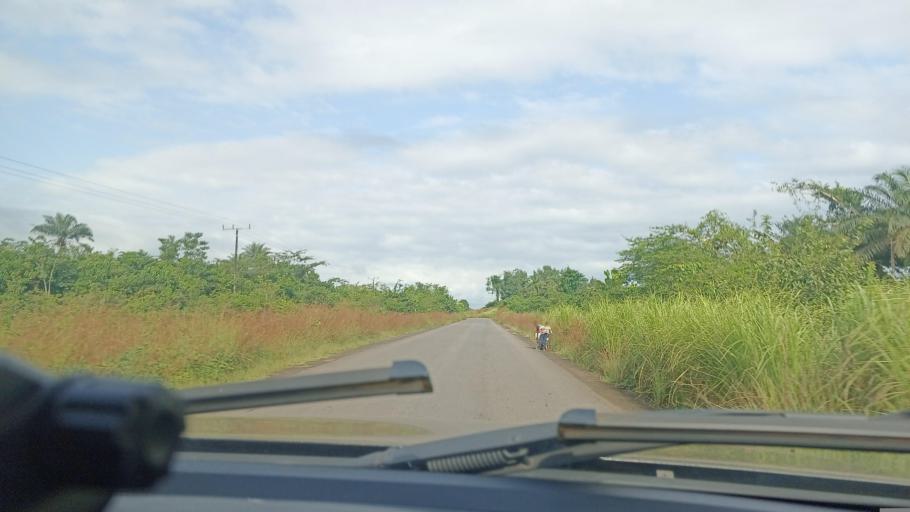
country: LR
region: Bomi
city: Tubmanburg
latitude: 6.7001
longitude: -10.9134
